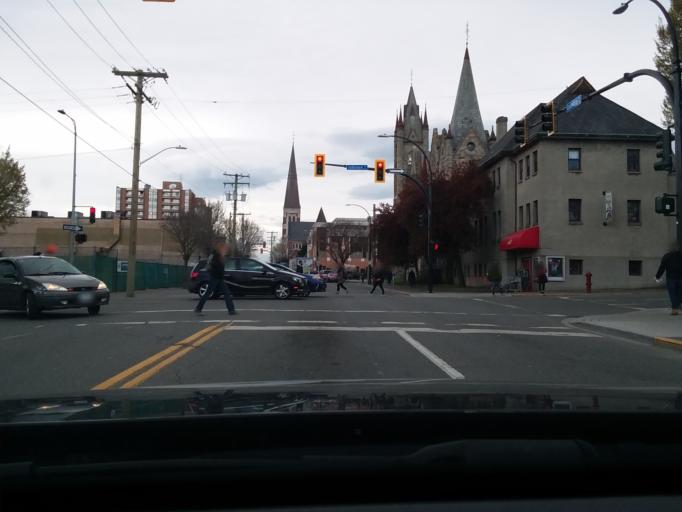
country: CA
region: British Columbia
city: Victoria
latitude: 48.4264
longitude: -123.3591
